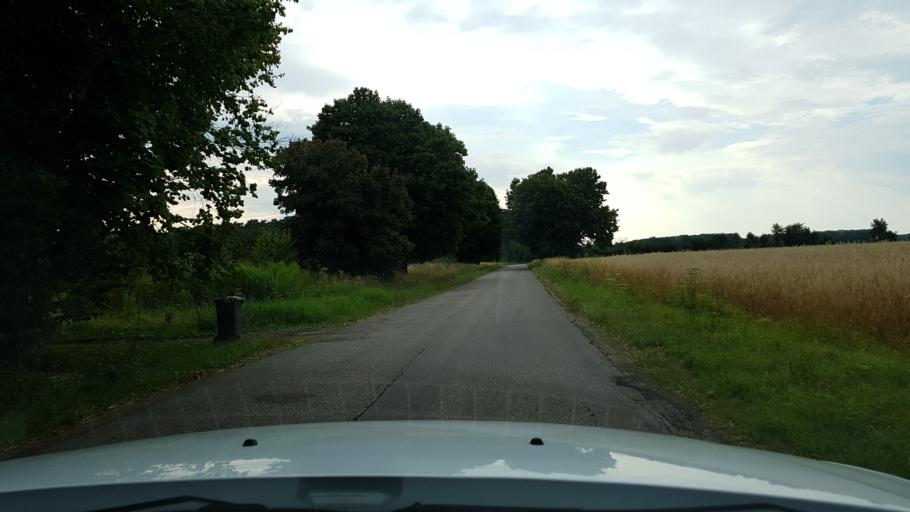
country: PL
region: West Pomeranian Voivodeship
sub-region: Powiat drawski
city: Wierzchowo
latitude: 53.4671
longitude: 16.0808
